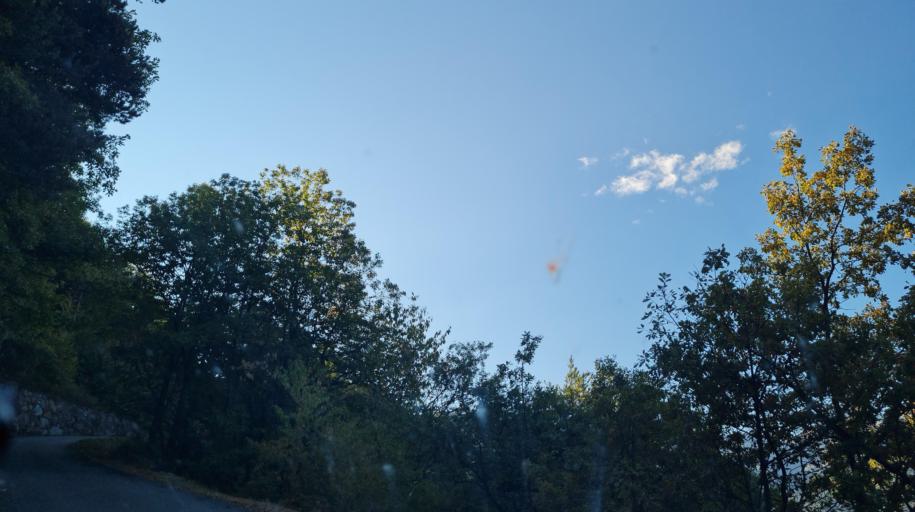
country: IT
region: Aosta Valley
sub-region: Valle d'Aosta
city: Arnad
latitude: 45.6455
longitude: 7.7436
